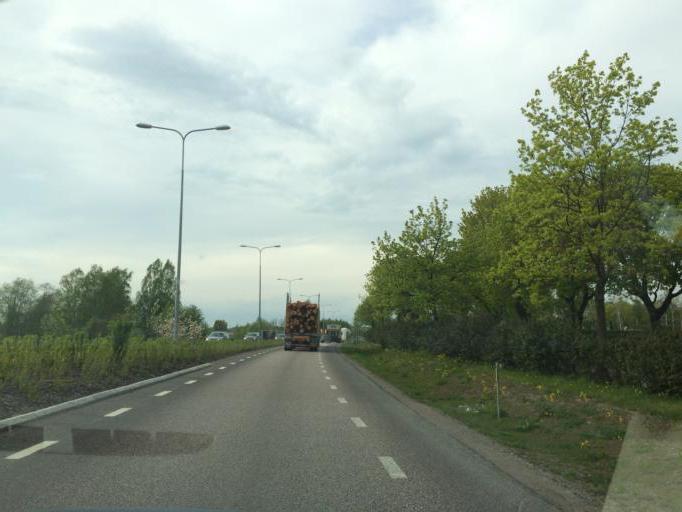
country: SE
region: Vaestmanland
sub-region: Kopings Kommun
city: Koping
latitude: 59.5133
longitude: 15.9819
